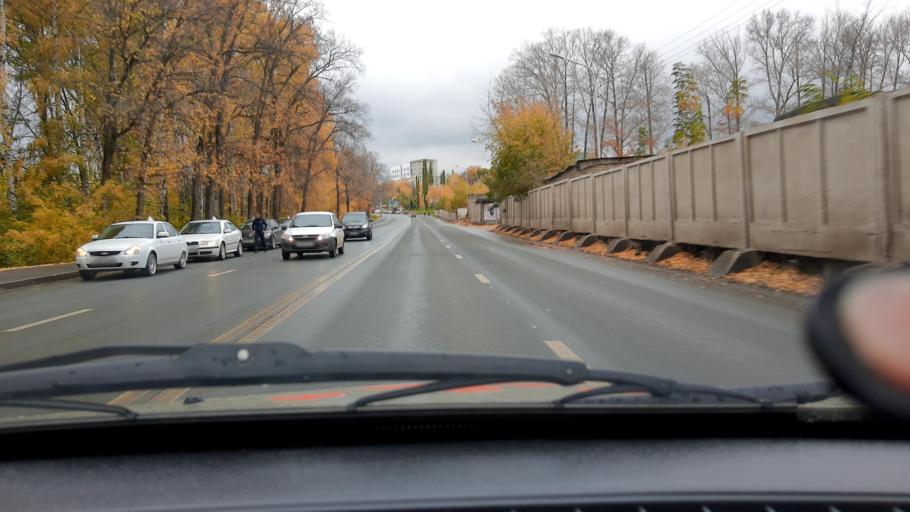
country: RU
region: Bashkortostan
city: Ufa
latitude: 54.8110
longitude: 56.0773
